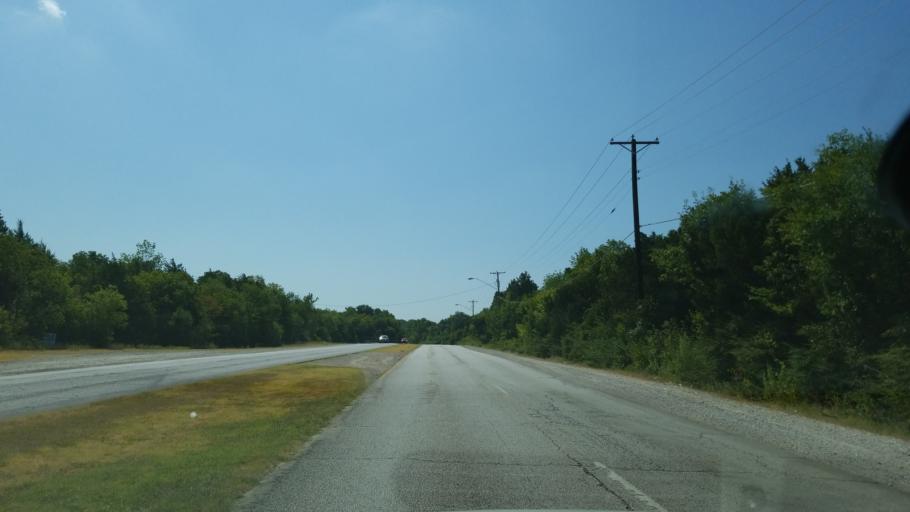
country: US
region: Texas
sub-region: Dallas County
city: Cockrell Hill
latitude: 32.7402
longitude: -96.9009
